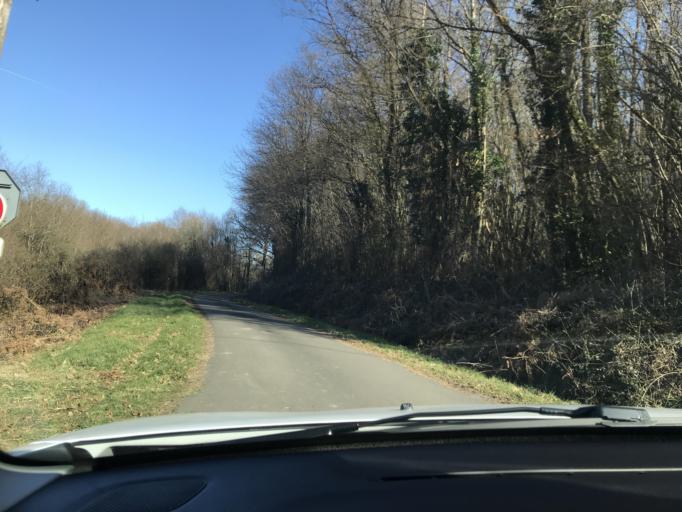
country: FR
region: Poitou-Charentes
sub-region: Departement de la Charente
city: Chasseneuil-sur-Bonnieure
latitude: 45.8459
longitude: 0.5113
